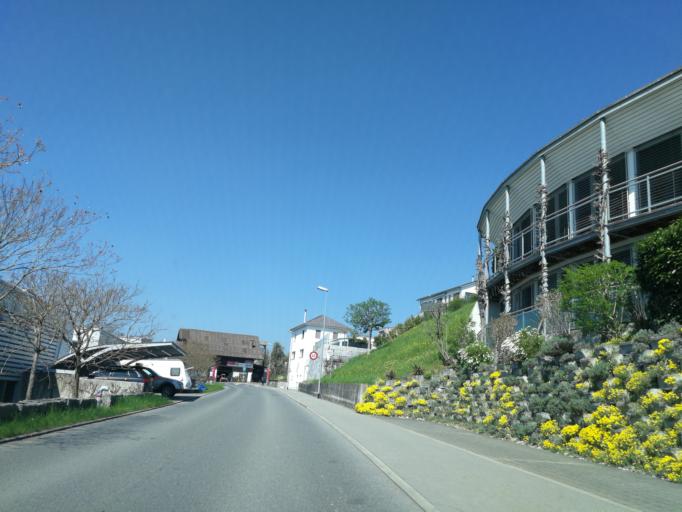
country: CH
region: Saint Gallen
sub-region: Wahlkreis See-Gaster
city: Rapperswil
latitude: 47.2441
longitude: 8.8197
